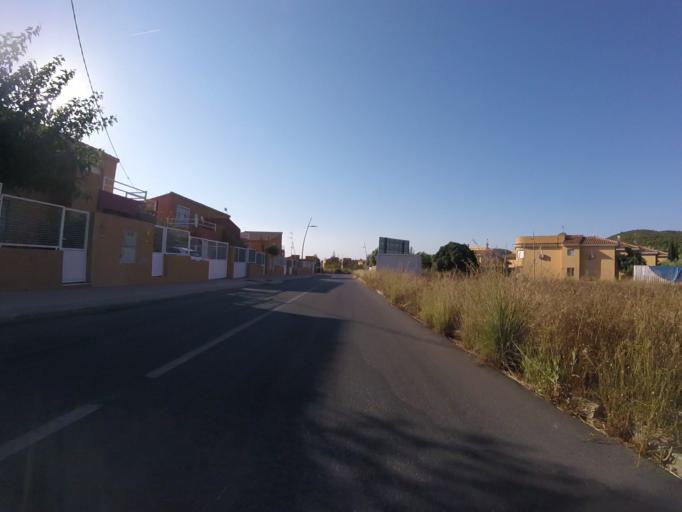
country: ES
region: Valencia
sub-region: Provincia de Castello
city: Peniscola
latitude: 40.3875
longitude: 0.3771
